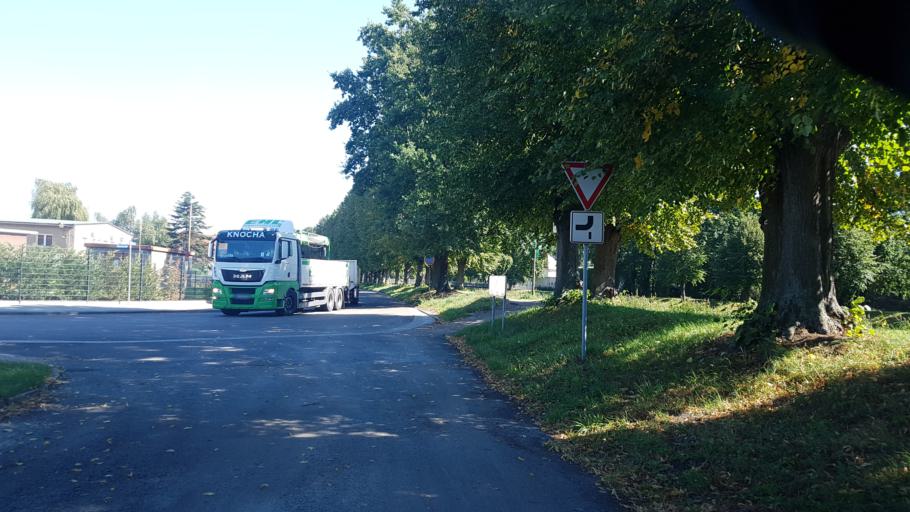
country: DE
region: Brandenburg
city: Elsterwerda
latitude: 51.4537
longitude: 13.5186
